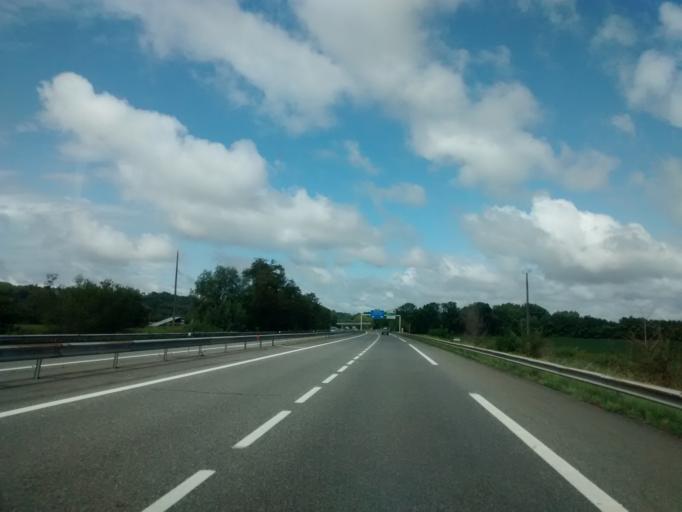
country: FR
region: Aquitaine
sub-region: Departement des Pyrenees-Atlantiques
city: Orthez
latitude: 43.4674
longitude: -0.7397
